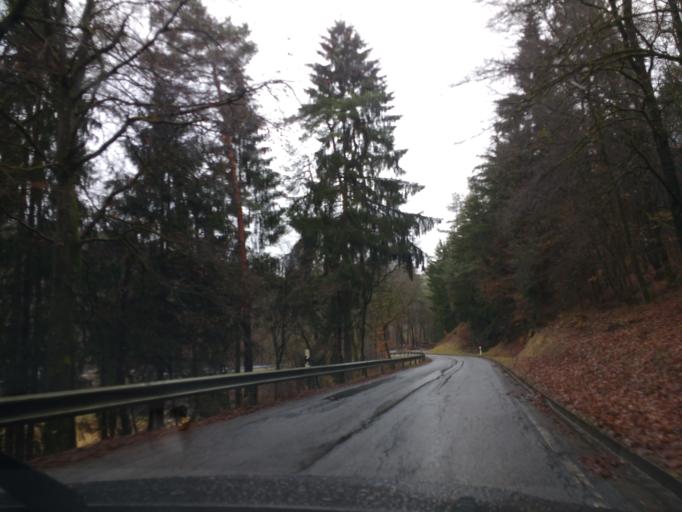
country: DE
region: Rheinland-Pfalz
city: Burtscheid
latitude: 49.7268
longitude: 6.9415
